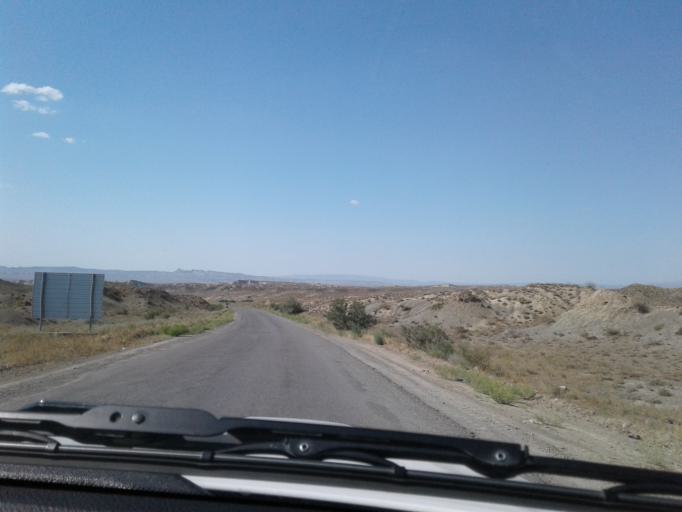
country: TM
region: Balkan
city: Magtymguly
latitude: 38.5033
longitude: 56.1931
